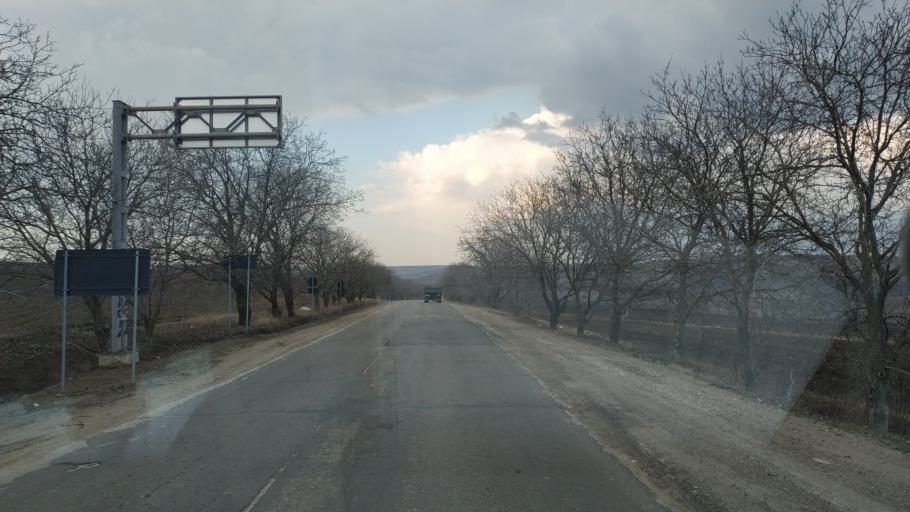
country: MD
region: Anenii Noi
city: Anenii Noi
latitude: 46.9287
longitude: 29.2874
